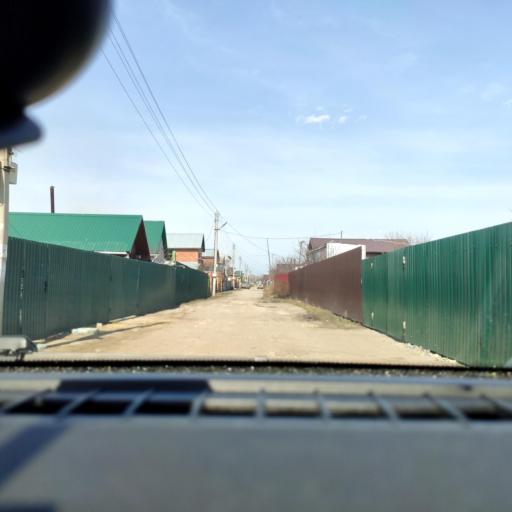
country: RU
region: Samara
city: Podstepki
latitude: 53.5133
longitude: 49.1066
